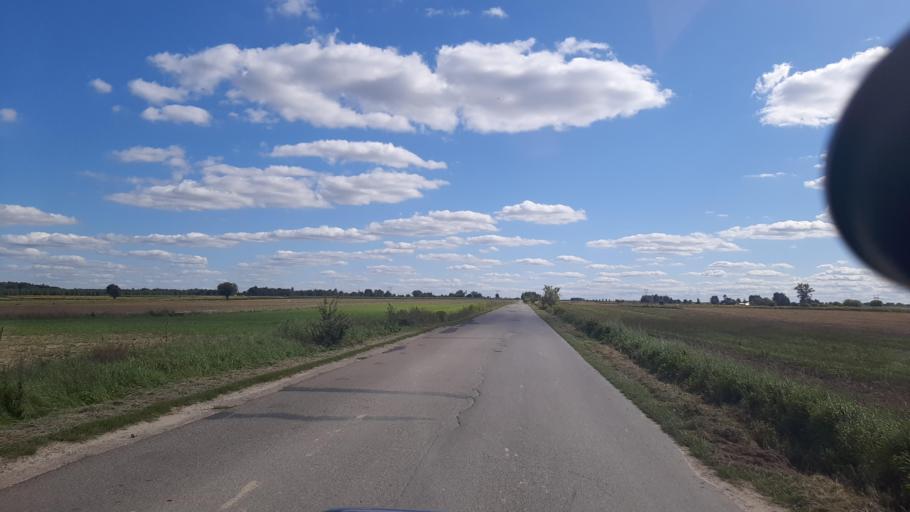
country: PL
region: Lublin Voivodeship
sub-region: Powiat pulawski
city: Markuszow
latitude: 51.4085
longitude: 22.2323
